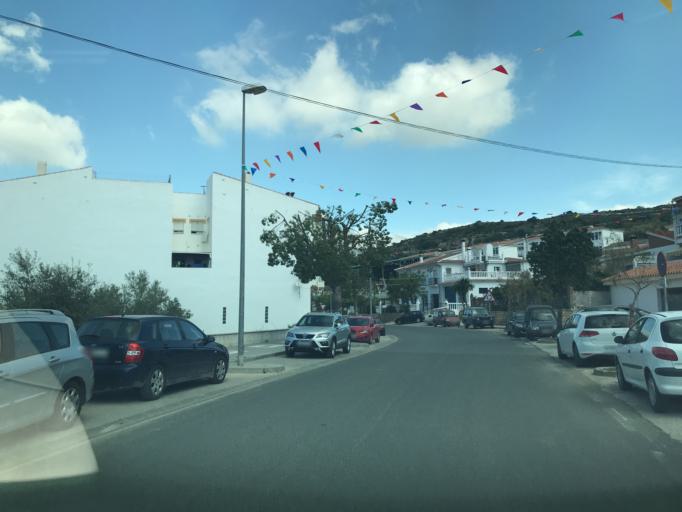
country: ES
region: Andalusia
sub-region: Provincia de Malaga
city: Periana
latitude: 36.9262
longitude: -4.1854
